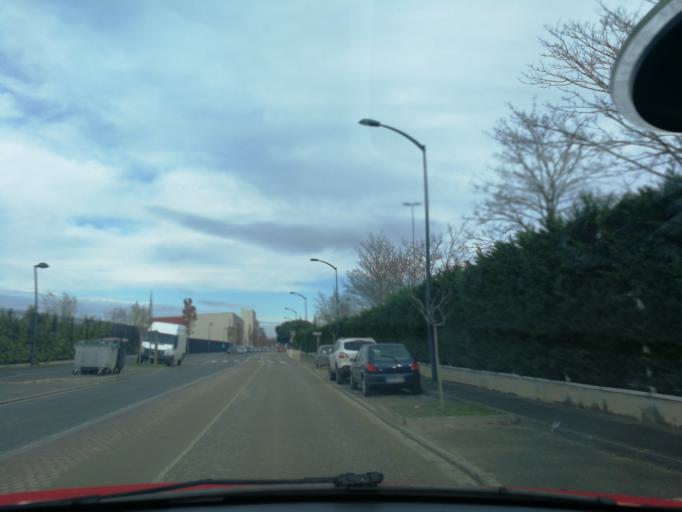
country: FR
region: Midi-Pyrenees
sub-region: Departement de la Haute-Garonne
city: Balma
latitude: 43.6231
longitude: 1.4876
